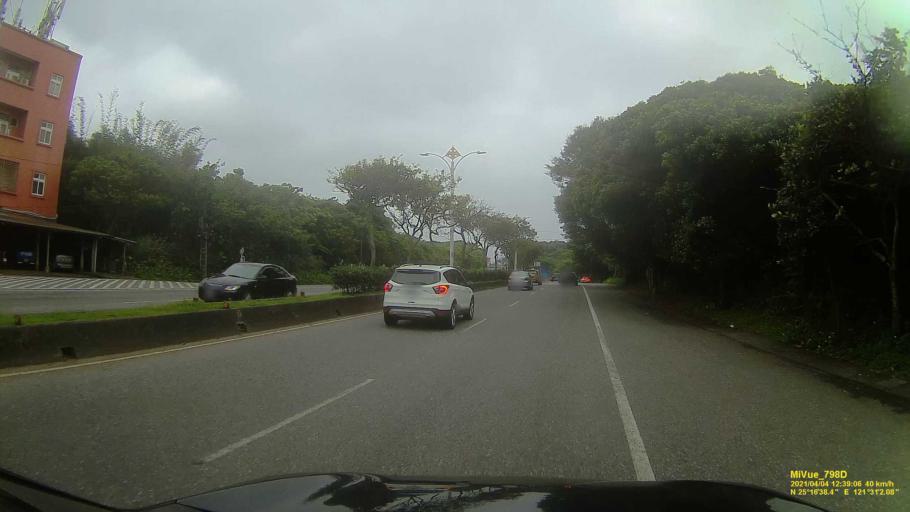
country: TW
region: Taipei
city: Taipei
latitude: 25.2772
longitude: 121.5172
